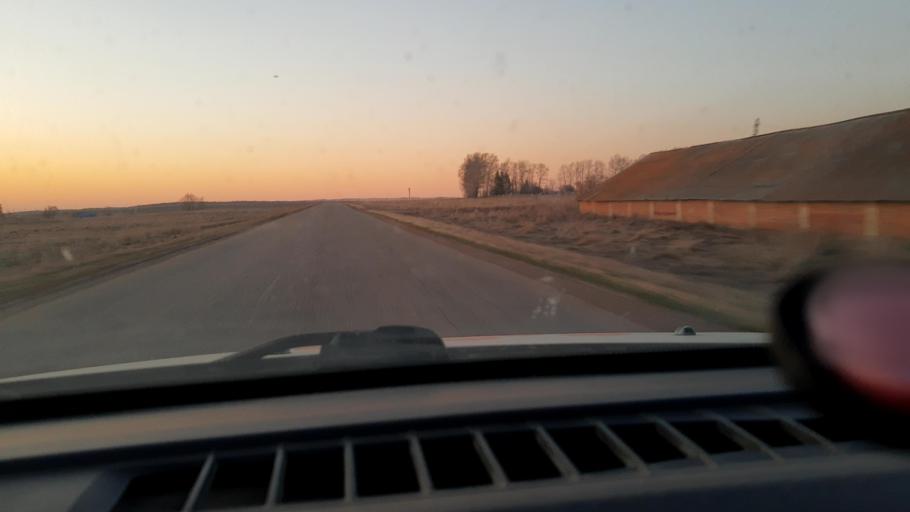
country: RU
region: Bashkortostan
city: Asanovo
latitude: 54.7928
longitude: 55.4988
